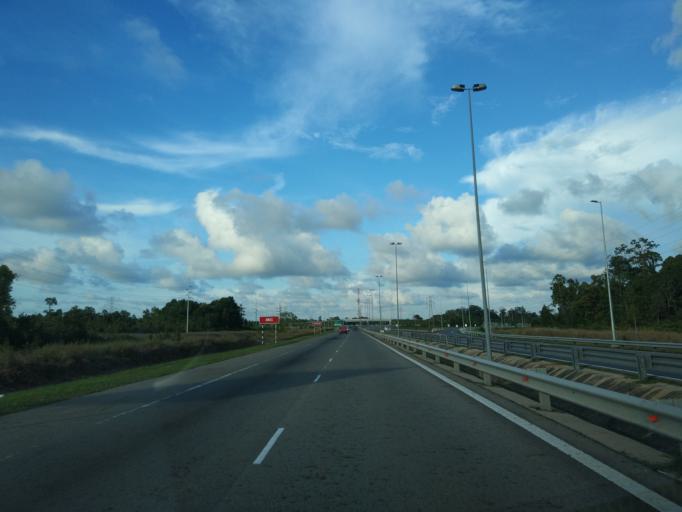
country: BN
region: Tutong
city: Tutong
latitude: 4.7413
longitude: 114.5942
